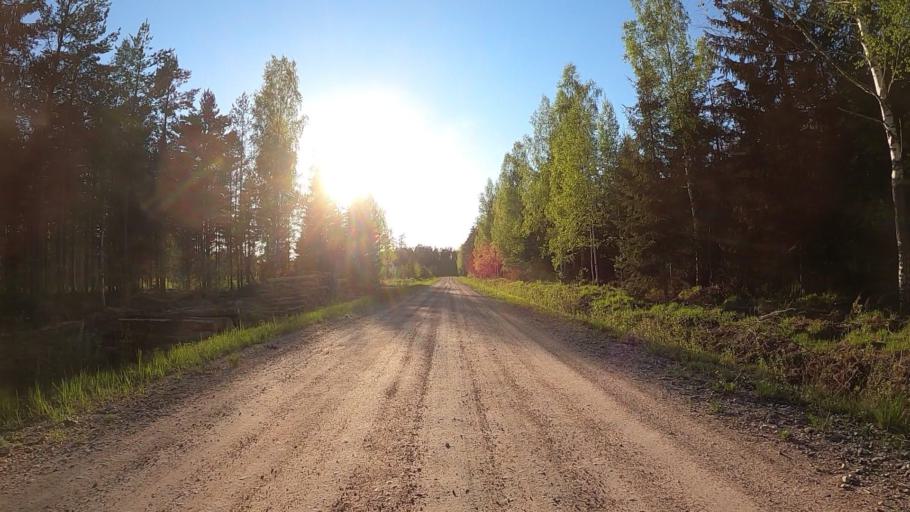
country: LV
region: Kekava
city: Kekava
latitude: 56.7571
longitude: 24.2294
